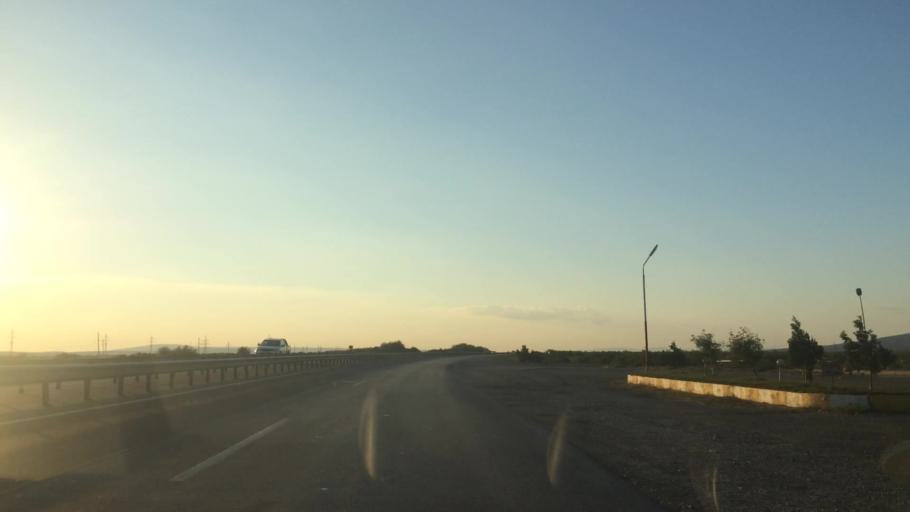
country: AZ
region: Baki
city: Qobustan
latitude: 39.9484
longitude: 49.3299
